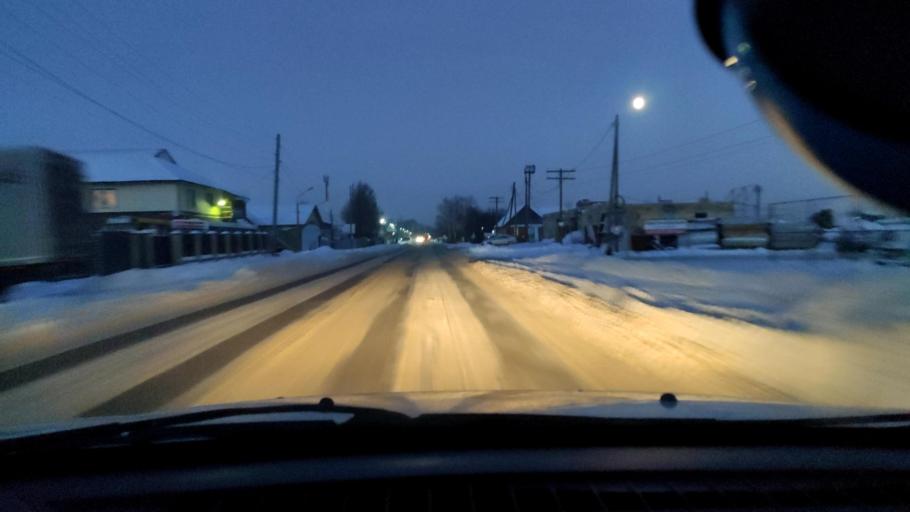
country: RU
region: Perm
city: Kultayevo
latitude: 57.8890
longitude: 55.9260
